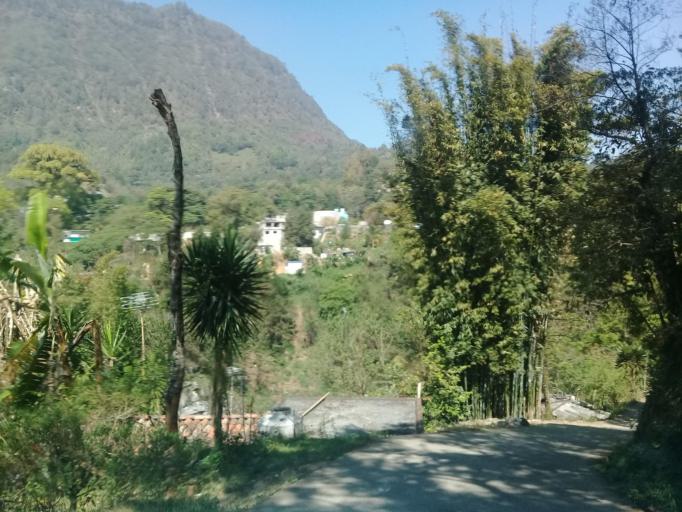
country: MX
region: Veracruz
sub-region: Tlilapan
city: Tonalixco
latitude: 18.7578
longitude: -97.0443
